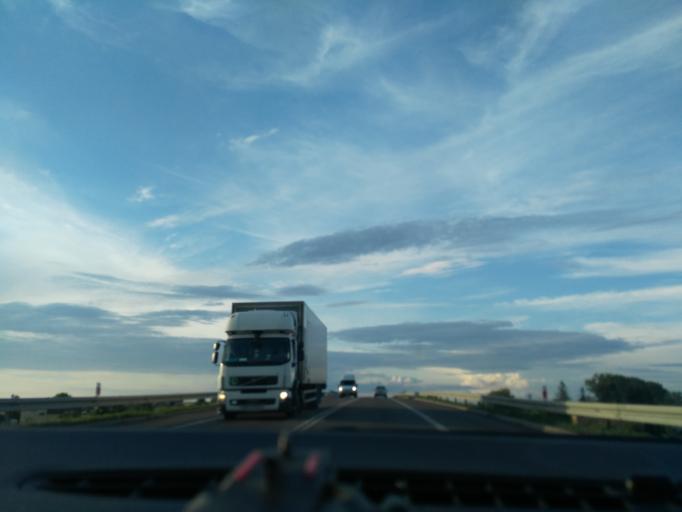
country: PL
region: Lublin Voivodeship
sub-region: Powiat lubelski
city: Niedrzwica Duza
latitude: 51.1262
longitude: 22.3923
